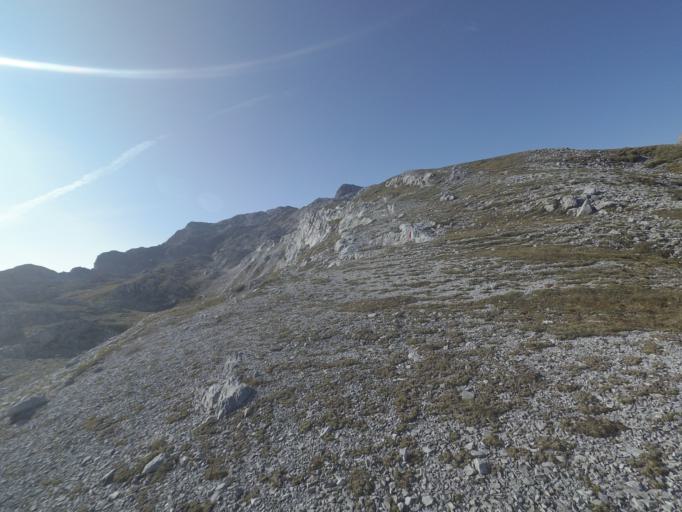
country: AT
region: Salzburg
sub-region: Politischer Bezirk Sankt Johann im Pongau
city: Kleinarl
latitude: 47.2212
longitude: 13.4054
